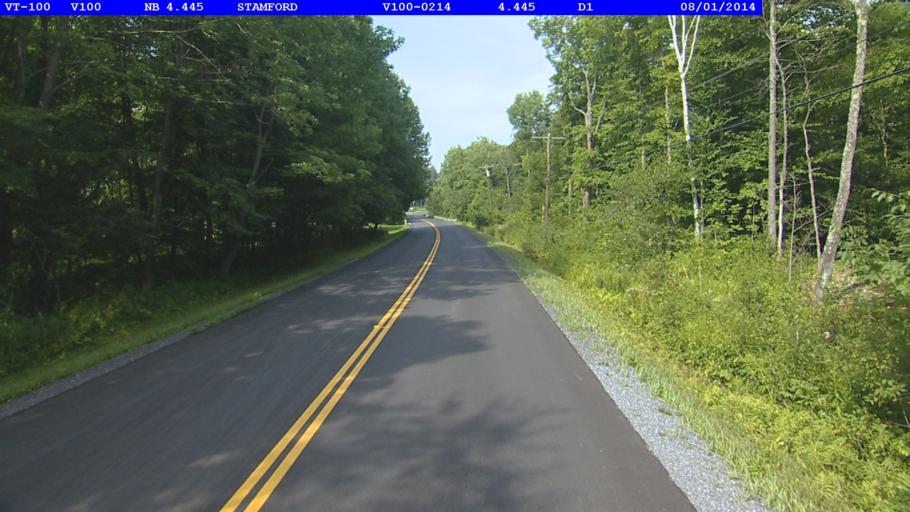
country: US
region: Massachusetts
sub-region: Berkshire County
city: North Adams
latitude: 42.7937
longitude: -73.0296
